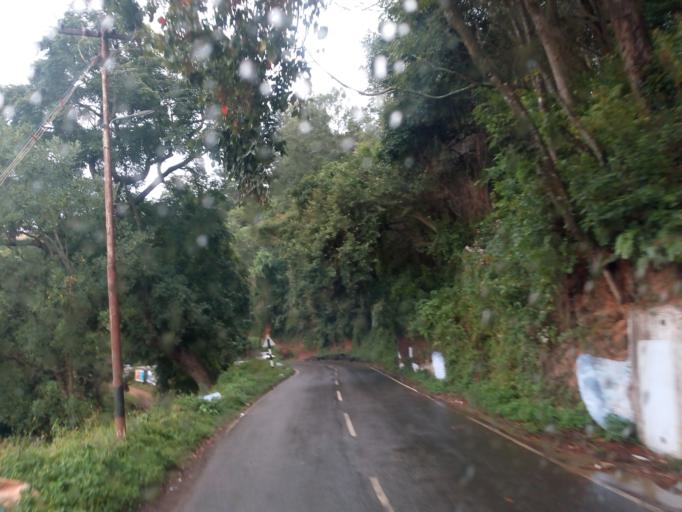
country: IN
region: Tamil Nadu
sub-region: Nilgiri
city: Wellington
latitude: 11.3419
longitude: 76.8008
